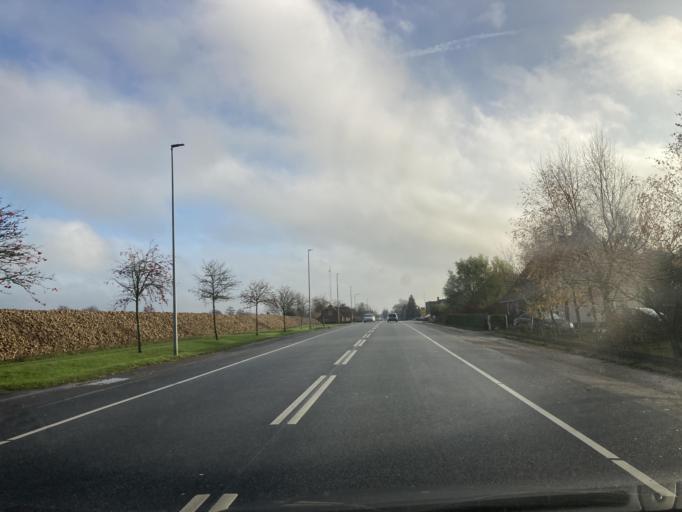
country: DK
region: Zealand
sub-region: Lolland Kommune
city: Maribo
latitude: 54.8084
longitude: 11.4234
